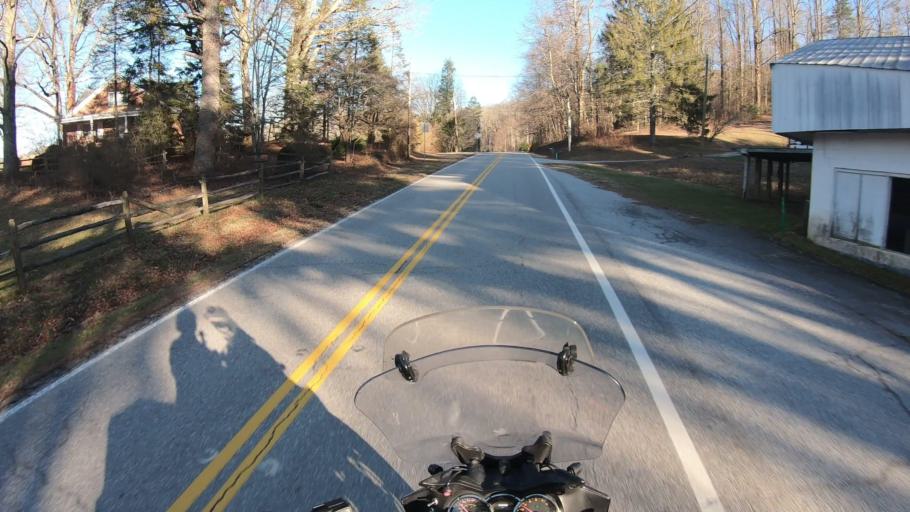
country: US
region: Georgia
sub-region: Lumpkin County
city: Dahlonega
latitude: 34.6944
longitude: -84.0217
